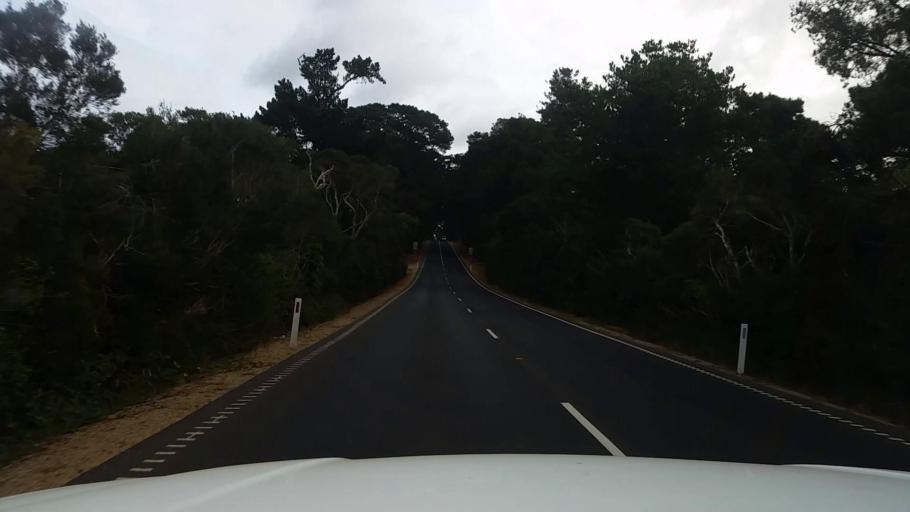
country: AU
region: Victoria
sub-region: Mornington Peninsula
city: Balnarring
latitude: -38.3608
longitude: 145.1140
